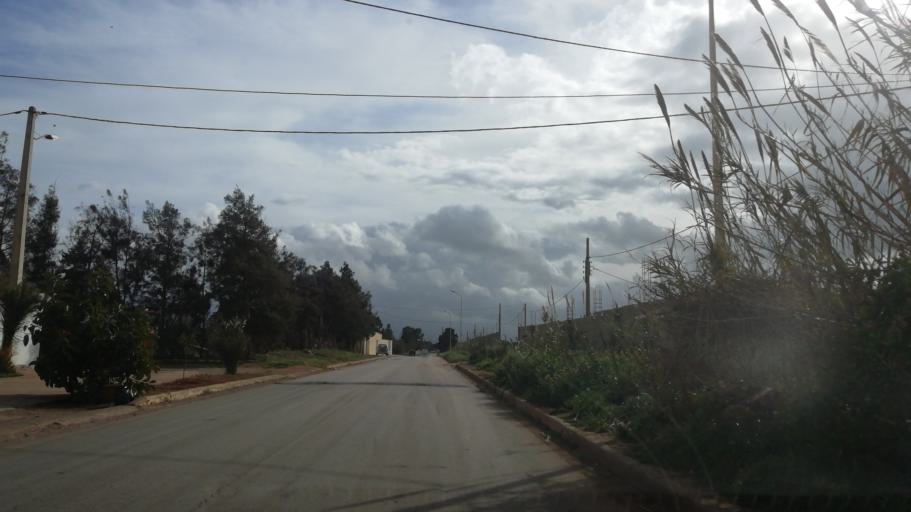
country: DZ
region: Oran
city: Es Senia
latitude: 35.6586
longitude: -0.6379
